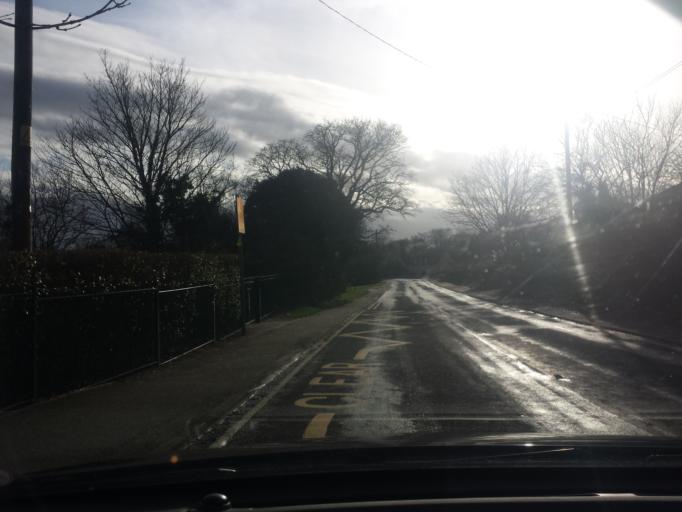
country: GB
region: England
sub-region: Essex
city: Alresford
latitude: 51.8949
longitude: 1.0271
